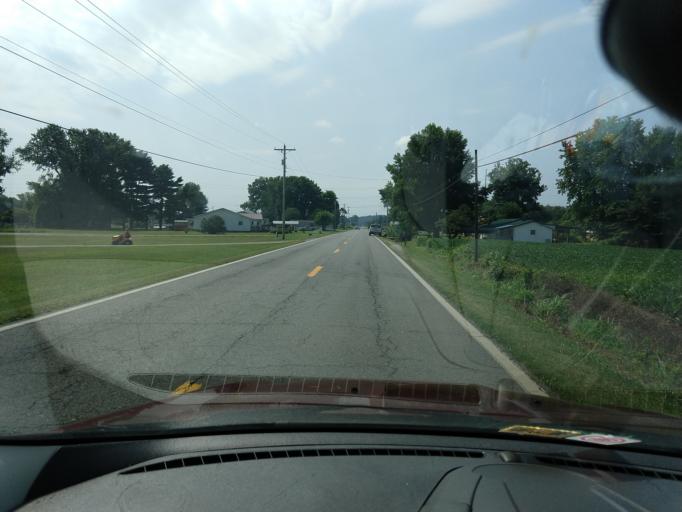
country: US
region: West Virginia
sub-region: Mason County
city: New Haven
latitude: 38.9538
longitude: -81.9222
